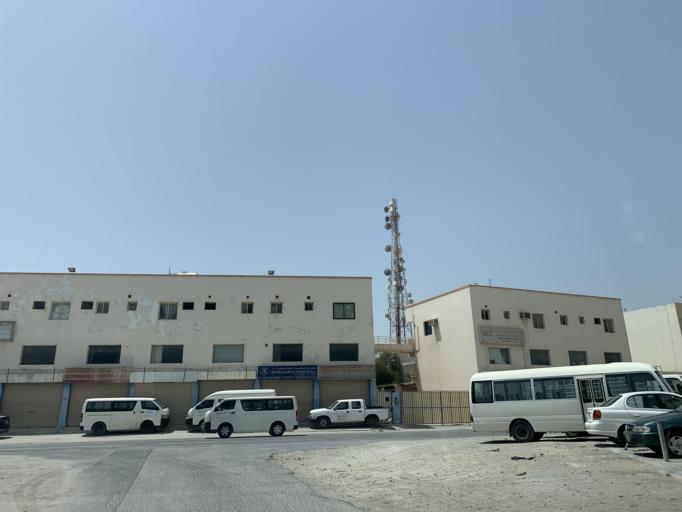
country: BH
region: Northern
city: Madinat `Isa
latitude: 26.1915
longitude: 50.5527
